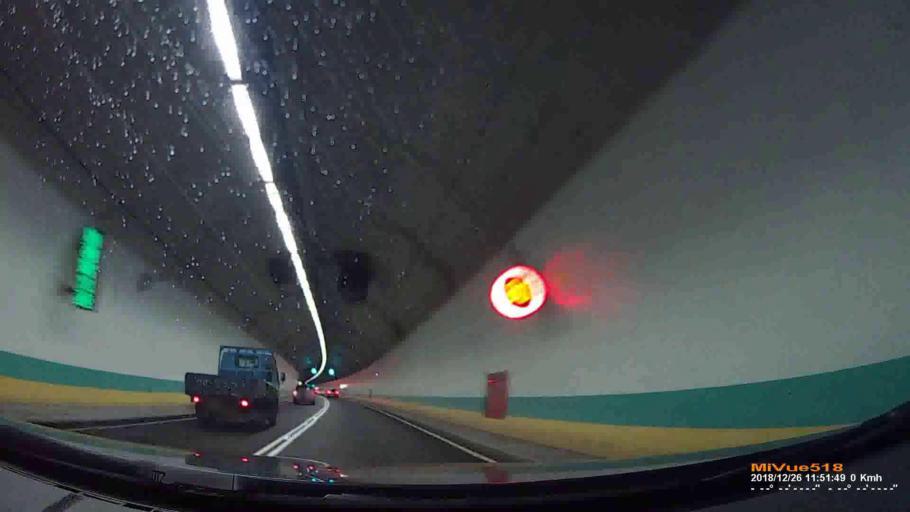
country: TW
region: Taipei
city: Taipei
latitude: 24.9719
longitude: 121.6799
